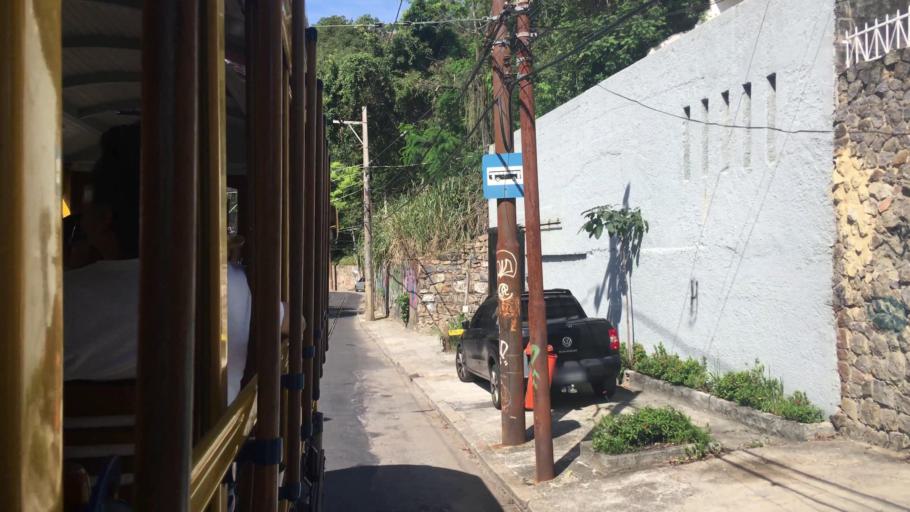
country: BR
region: Rio de Janeiro
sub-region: Rio De Janeiro
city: Rio de Janeiro
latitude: -22.9256
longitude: -43.1905
